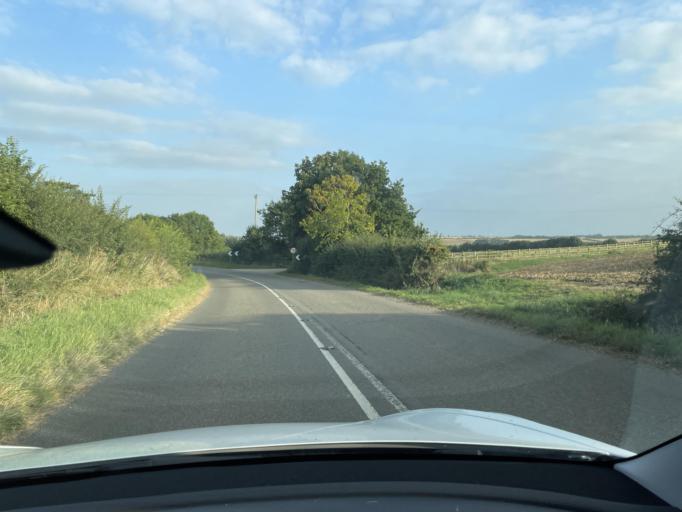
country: GB
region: England
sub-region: Northamptonshire
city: Raunds
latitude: 52.3706
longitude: -0.4537
